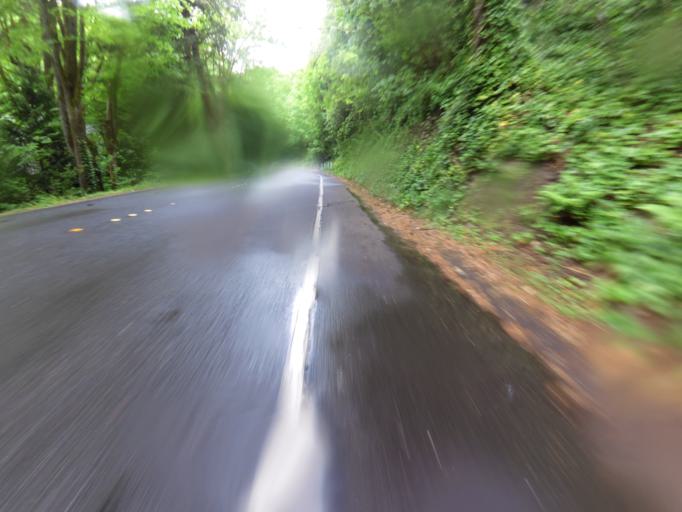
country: US
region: Washington
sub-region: King County
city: Mercer Island
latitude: 47.5450
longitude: -122.2139
